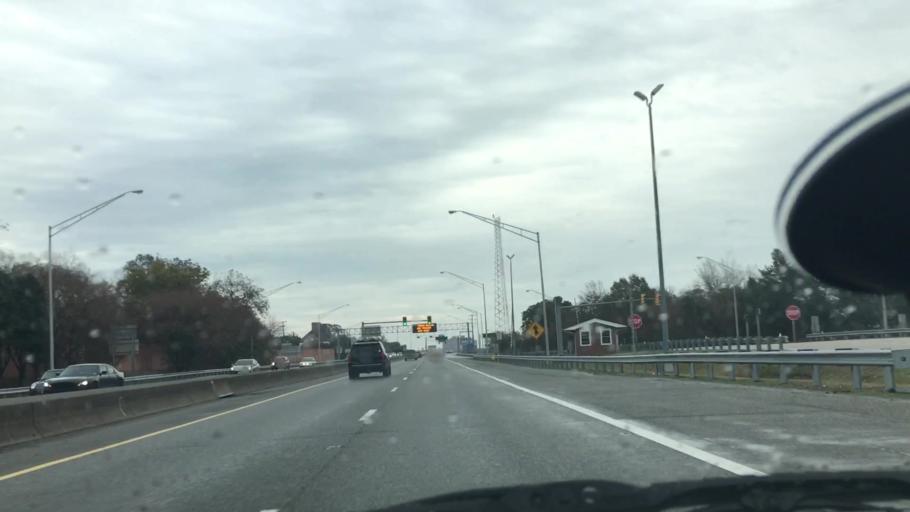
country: US
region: Virginia
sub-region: City of Hampton
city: East Hampton
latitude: 37.0152
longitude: -76.3265
